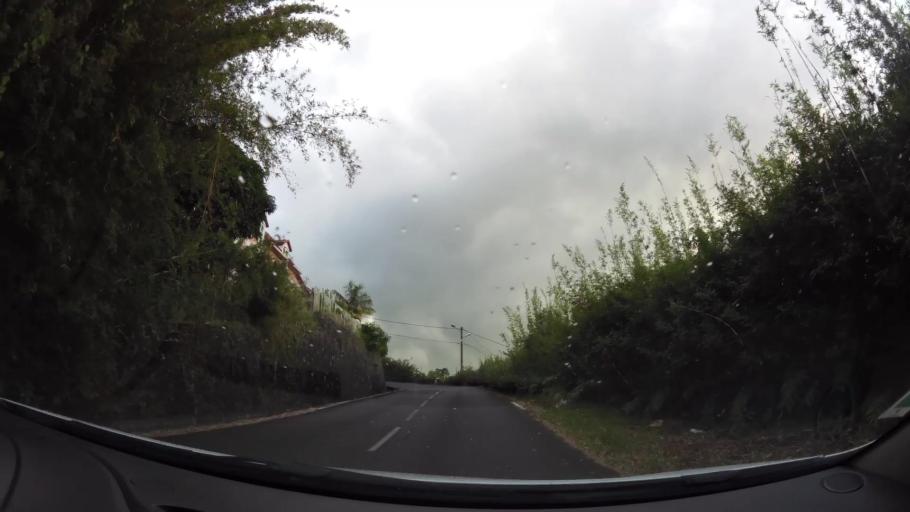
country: RE
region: Reunion
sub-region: Reunion
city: Saint-Denis
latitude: -20.9134
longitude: 55.4400
